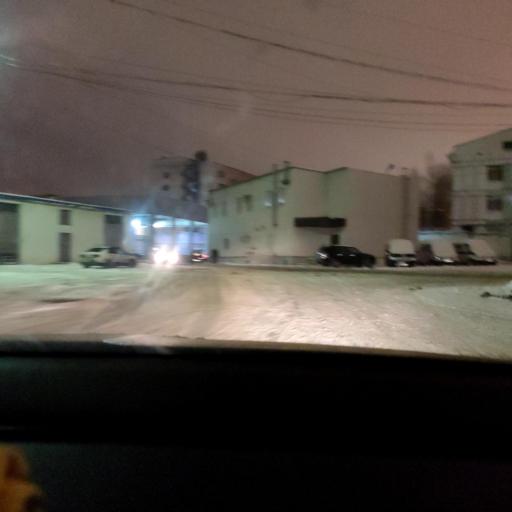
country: RU
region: Moscow
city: Rostokino
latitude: 55.8268
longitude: 37.6603
